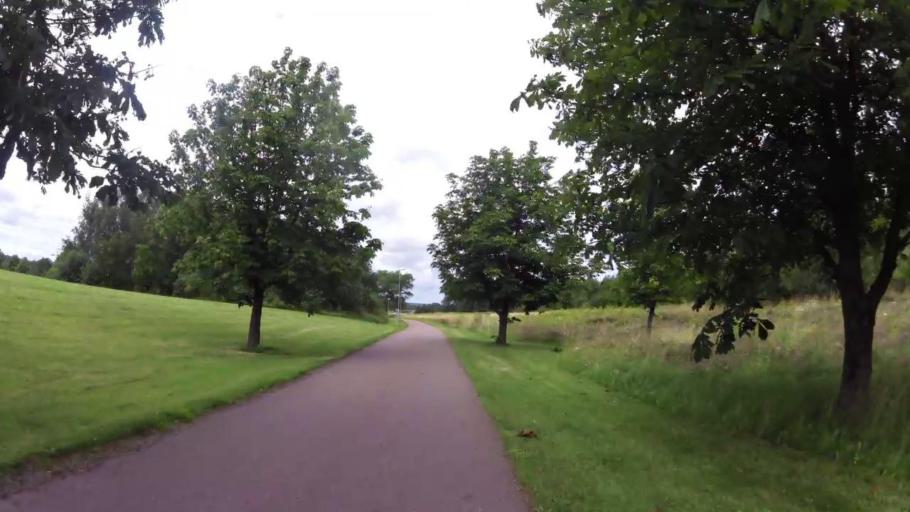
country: SE
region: OEstergoetland
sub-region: Linkopings Kommun
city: Linkoping
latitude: 58.4229
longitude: 15.5942
